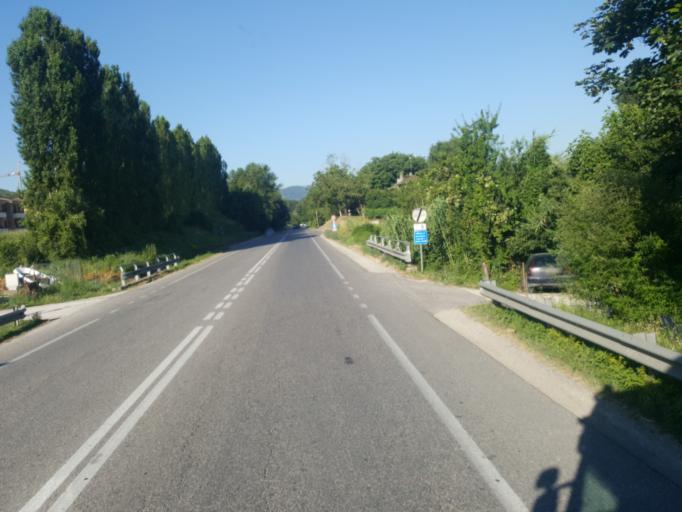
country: IT
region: The Marches
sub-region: Provincia di Pesaro e Urbino
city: Montelabbate
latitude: 43.8494
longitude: 12.7845
